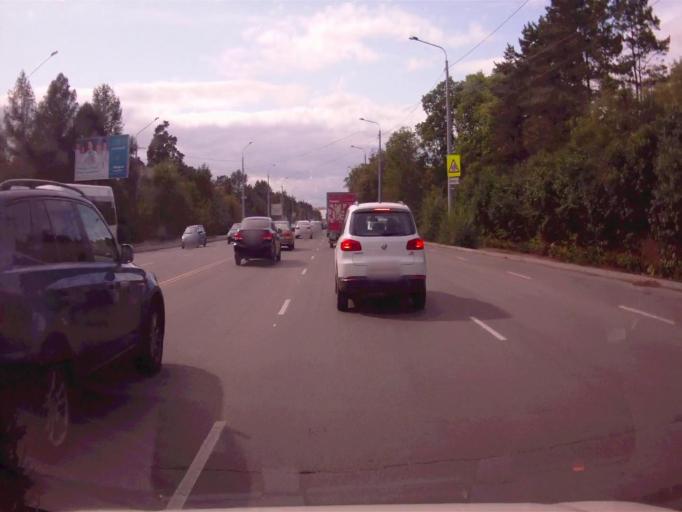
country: RU
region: Chelyabinsk
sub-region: Gorod Chelyabinsk
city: Chelyabinsk
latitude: 55.1473
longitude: 61.3616
